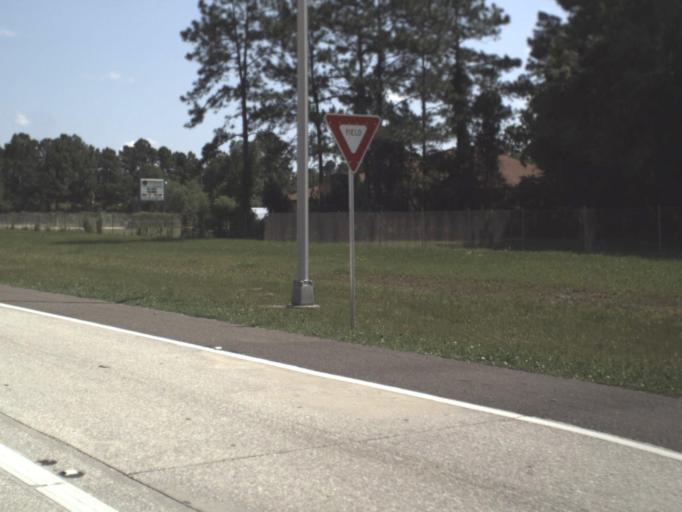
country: US
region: Florida
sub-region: Duval County
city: Jacksonville
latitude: 30.4121
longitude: -81.6571
